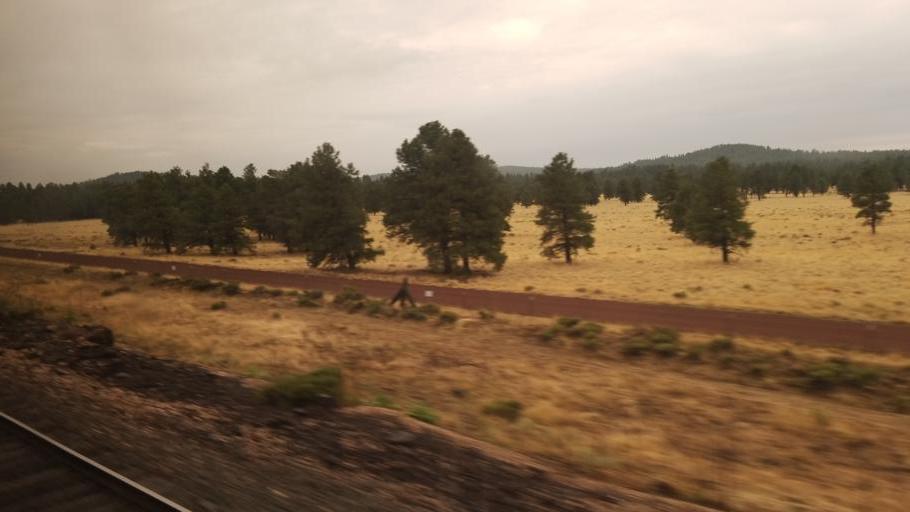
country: US
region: Arizona
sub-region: Coconino County
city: Flagstaff
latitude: 35.2226
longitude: -111.7989
